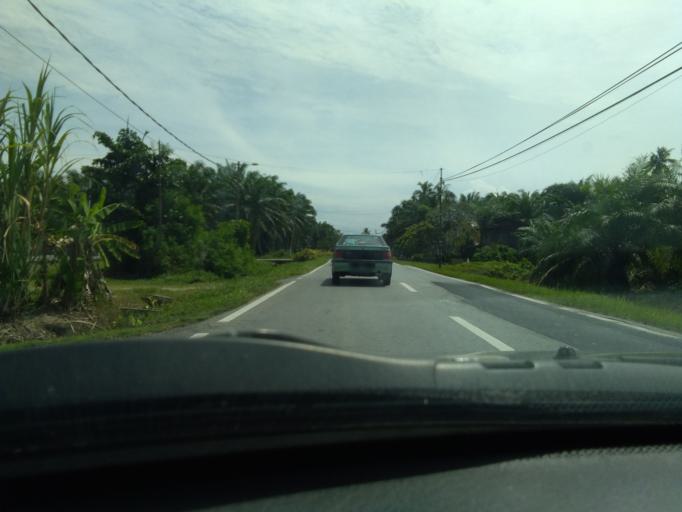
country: MY
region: Perak
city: Bagan Serai
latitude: 5.0295
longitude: 100.5590
